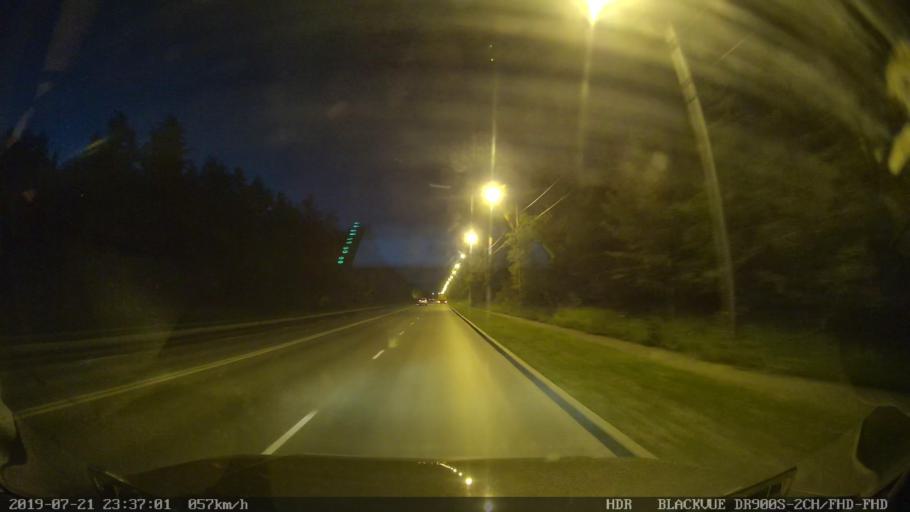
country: RU
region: Perm
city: Kondratovo
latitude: 57.9441
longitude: 56.1717
